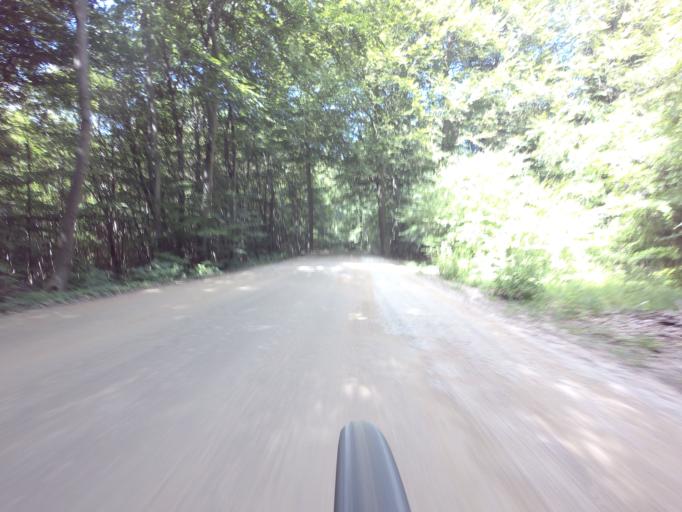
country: DK
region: Zealand
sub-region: Vordingborg Kommune
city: Stege
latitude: 54.9670
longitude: 12.5406
